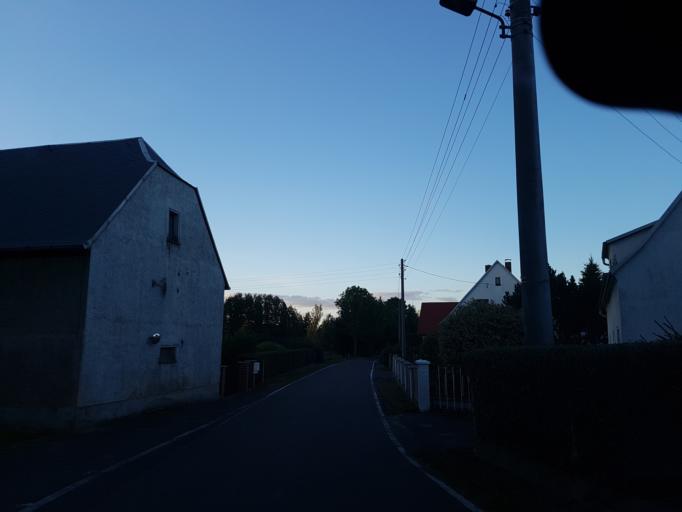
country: DE
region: Saxony
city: Oschatz
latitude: 51.2804
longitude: 13.1493
